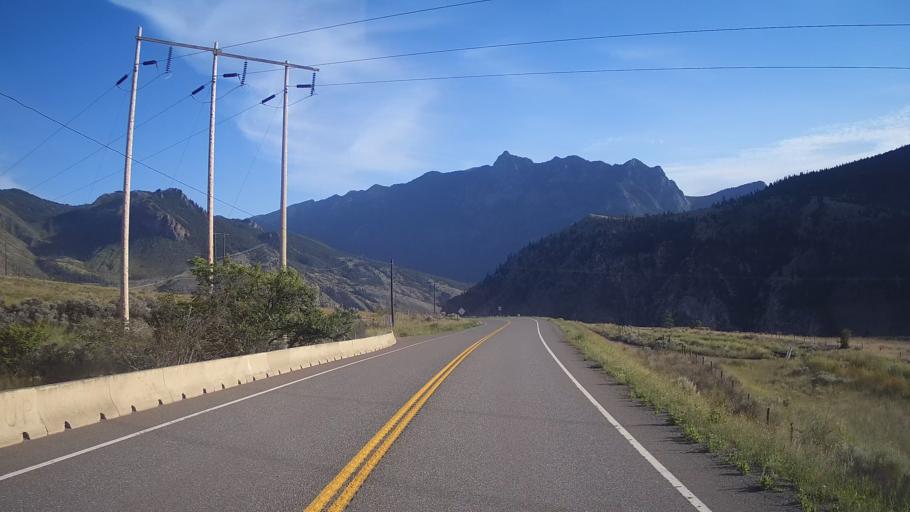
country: CA
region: British Columbia
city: Lillooet
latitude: 50.7757
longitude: -121.8385
